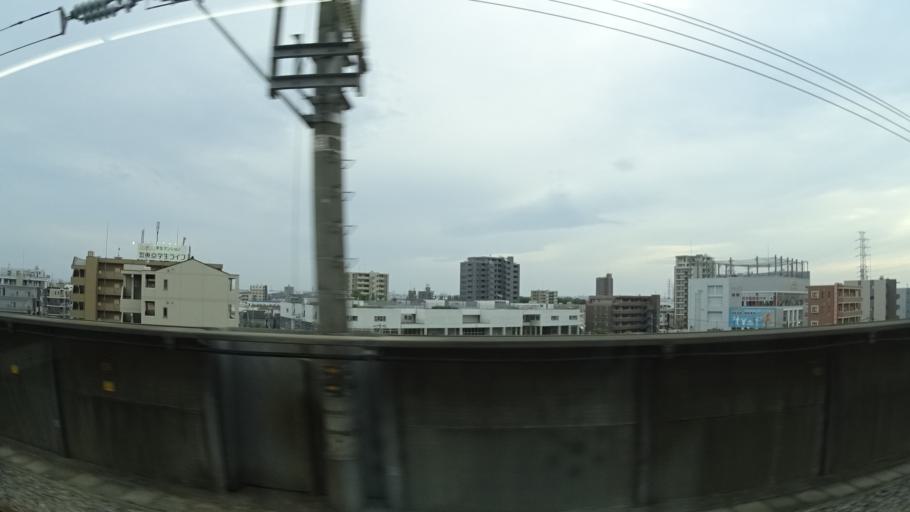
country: JP
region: Saitama
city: Shimotoda
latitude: 35.8260
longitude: 139.6626
